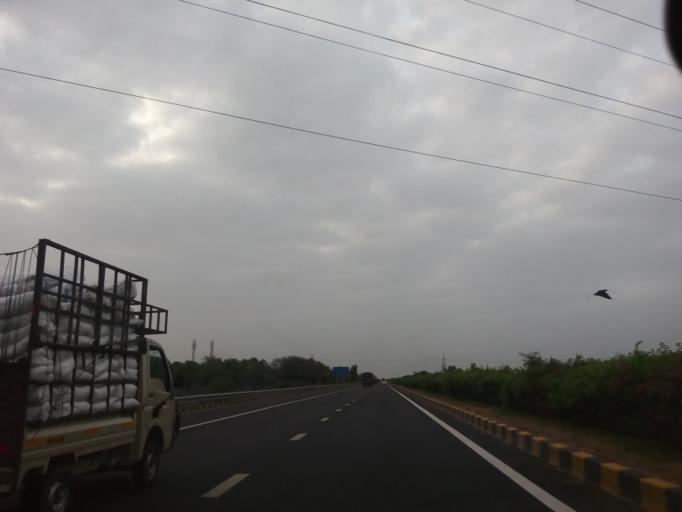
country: IN
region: Gujarat
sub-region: Kheda
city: Mahemdavad
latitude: 22.9383
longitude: 72.7181
